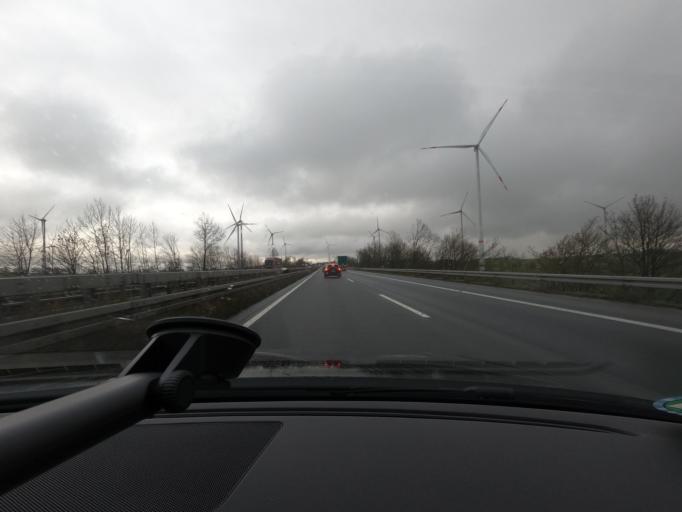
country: DE
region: North Rhine-Westphalia
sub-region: Regierungsbezirk Detmold
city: Wunnenberg
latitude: 51.5575
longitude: 8.7775
